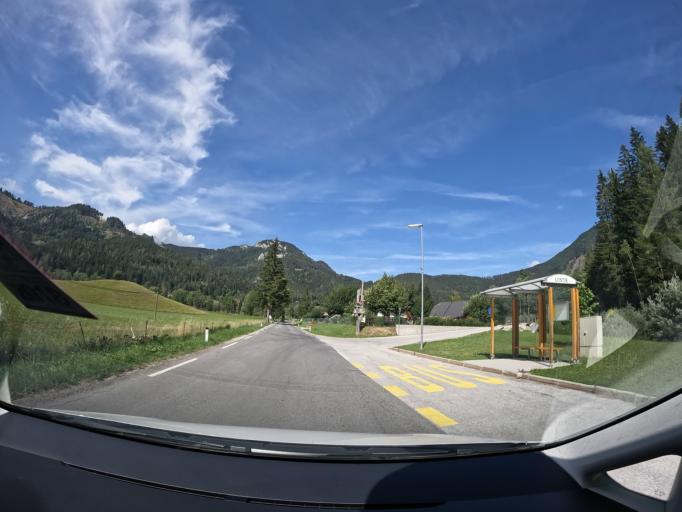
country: AT
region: Carinthia
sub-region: Politischer Bezirk Feldkirchen
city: Feldkirchen in Karnten
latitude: 46.7131
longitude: 14.1290
